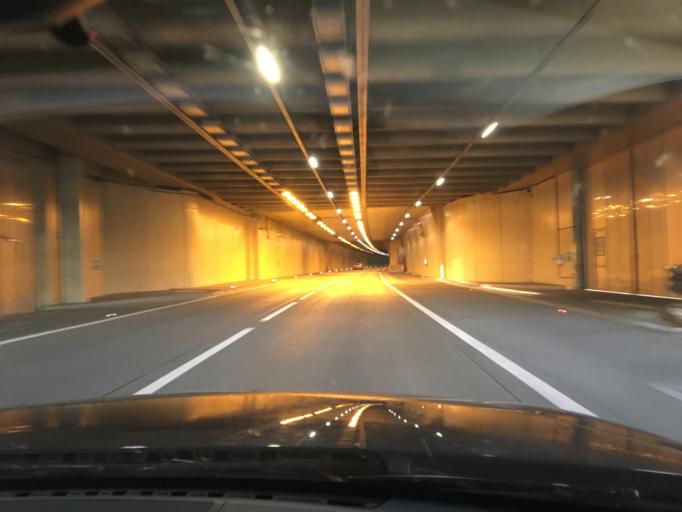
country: AT
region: Vorarlberg
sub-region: Politischer Bezirk Bregenz
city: Lochau
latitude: 47.5390
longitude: 9.7575
